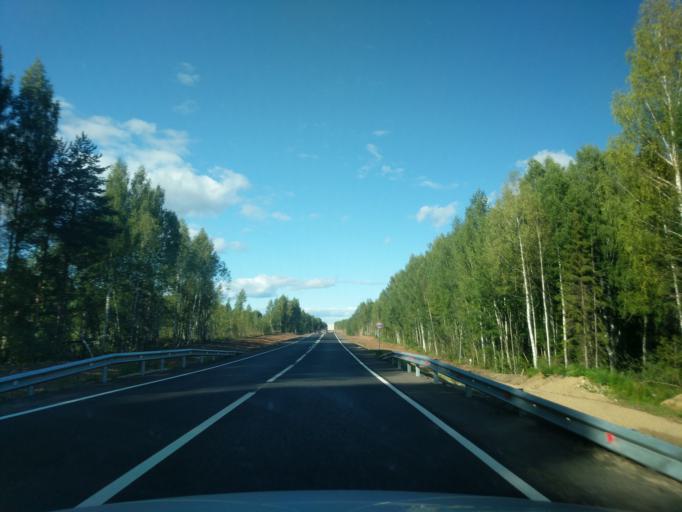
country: RU
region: Kostroma
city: Makar'yev
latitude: 57.9828
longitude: 43.9593
